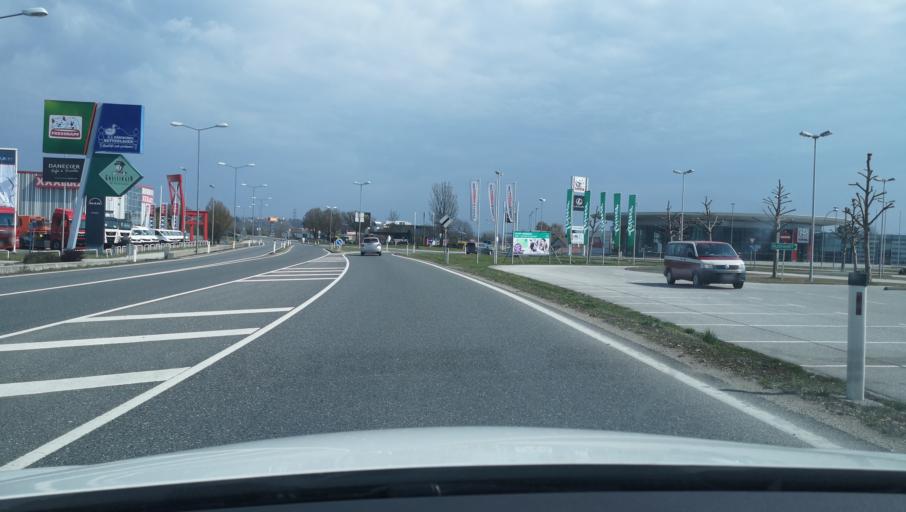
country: AT
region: Lower Austria
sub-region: Politischer Bezirk Amstetten
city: Winklarn
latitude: 48.1074
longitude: 14.8345
